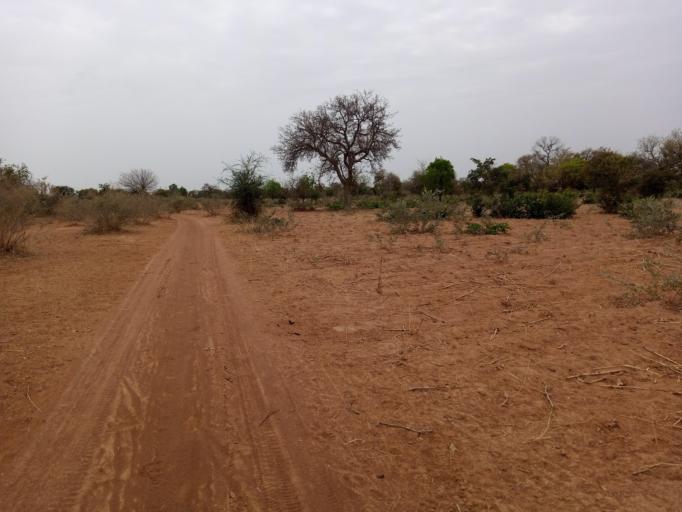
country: BF
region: Boucle du Mouhoun
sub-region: Province de la Kossi
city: Nouna
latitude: 12.8490
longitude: -4.0774
